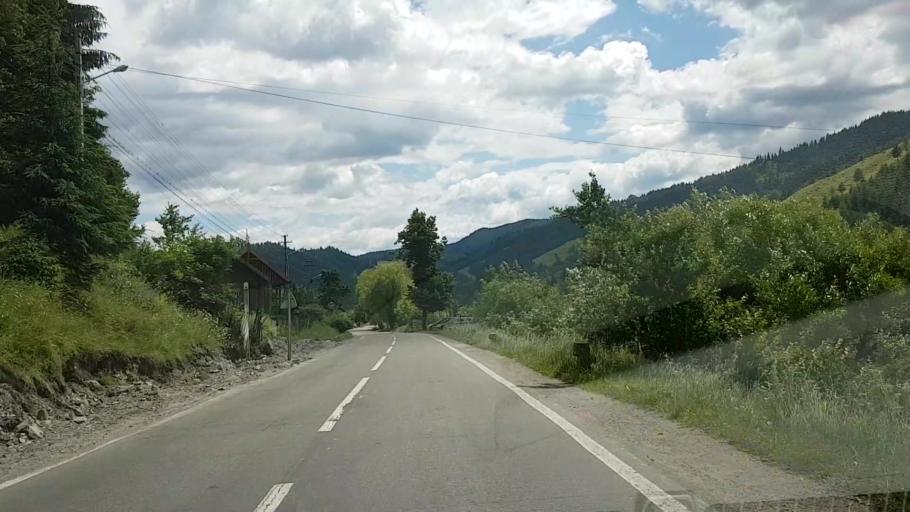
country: RO
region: Suceava
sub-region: Comuna Brosteni
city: Brosteni
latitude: 47.2427
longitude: 25.7059
